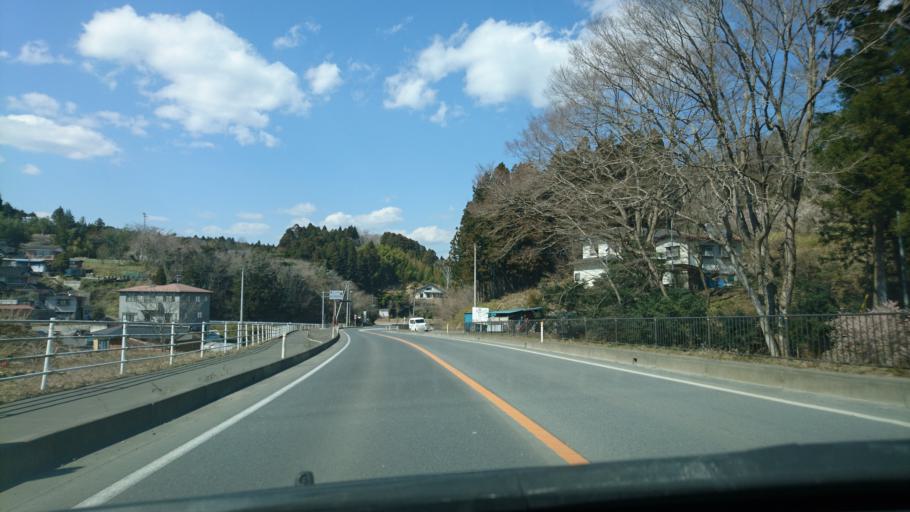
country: JP
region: Miyagi
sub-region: Oshika Gun
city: Onagawa Cho
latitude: 38.6690
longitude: 141.4410
